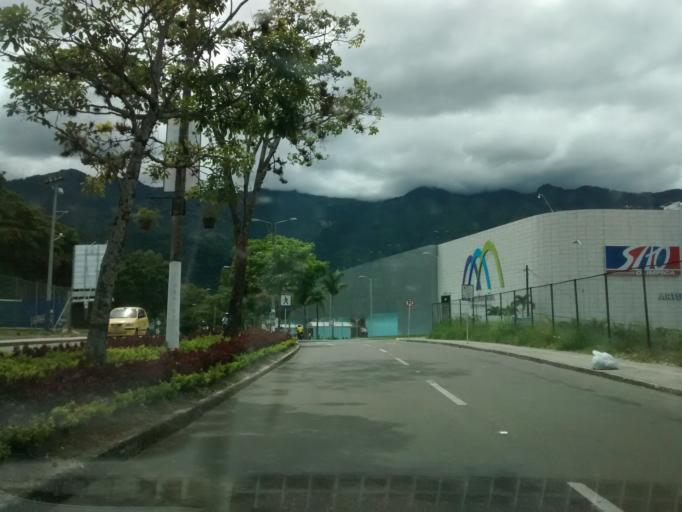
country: CO
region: Tolima
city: Ibague
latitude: 4.4442
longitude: -75.2050
